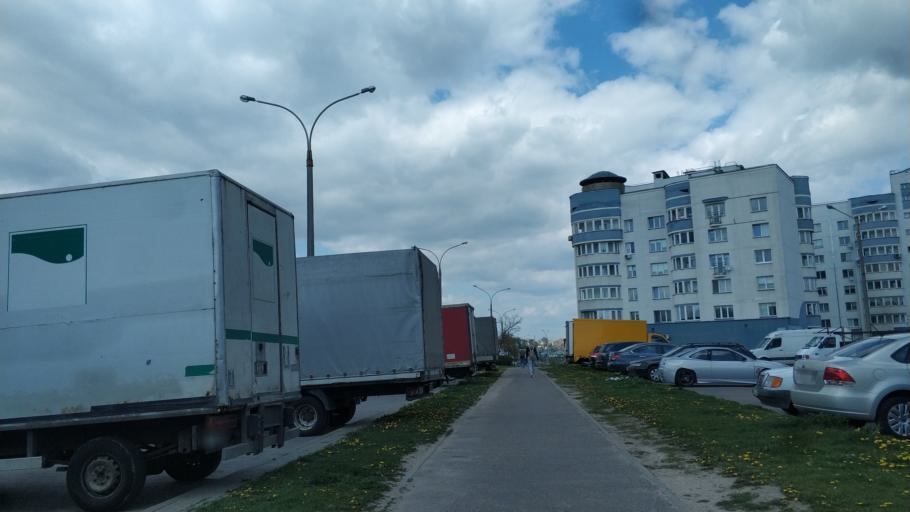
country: BY
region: Minsk
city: Syenitsa
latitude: 53.8381
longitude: 27.5657
